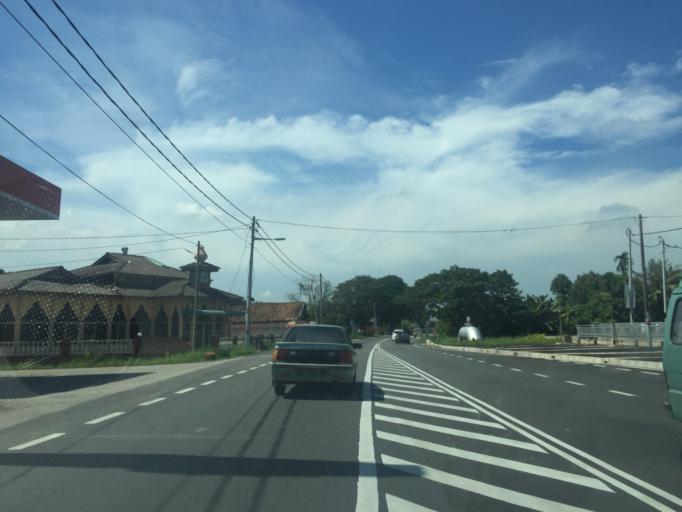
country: MY
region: Penang
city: Permatang Kuching
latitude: 5.4542
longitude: 100.4396
